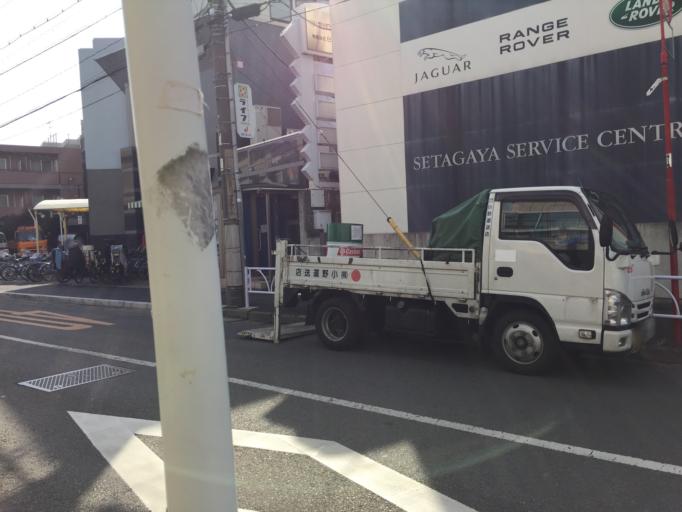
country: JP
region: Tokyo
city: Tokyo
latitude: 35.6323
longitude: 139.6387
